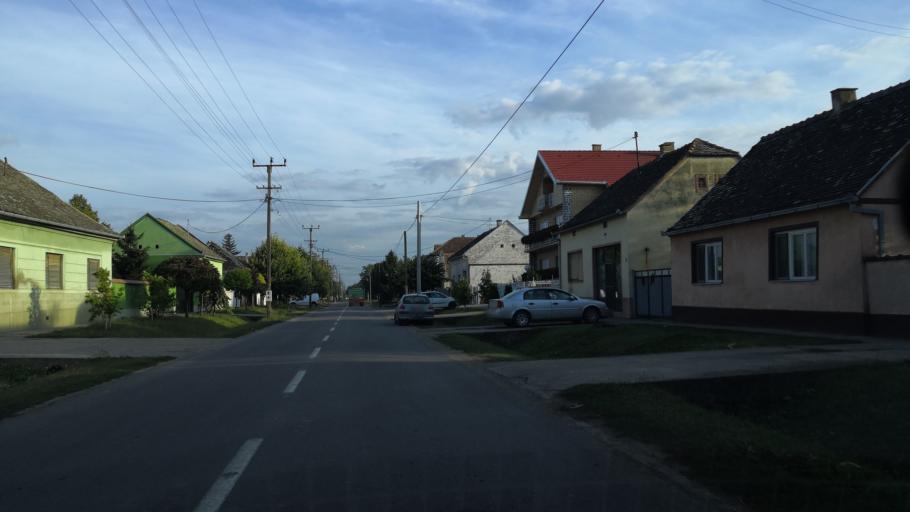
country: RS
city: Novi Karlovci
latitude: 45.0765
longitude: 20.1805
